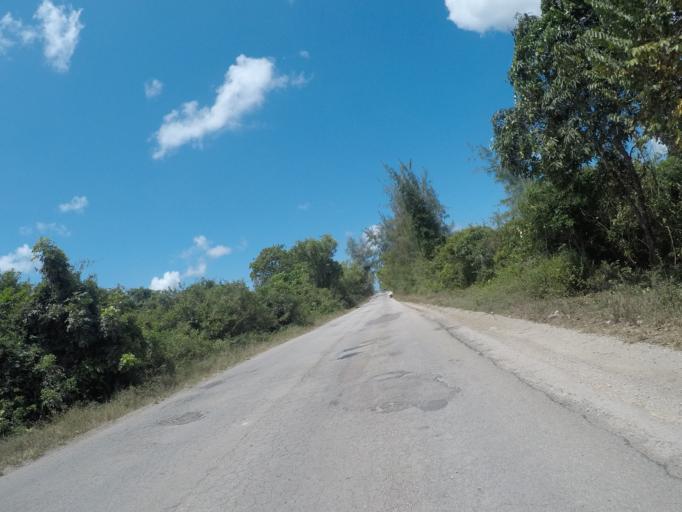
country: TZ
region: Zanzibar Central/South
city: Nganane
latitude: -6.2876
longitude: 39.4444
